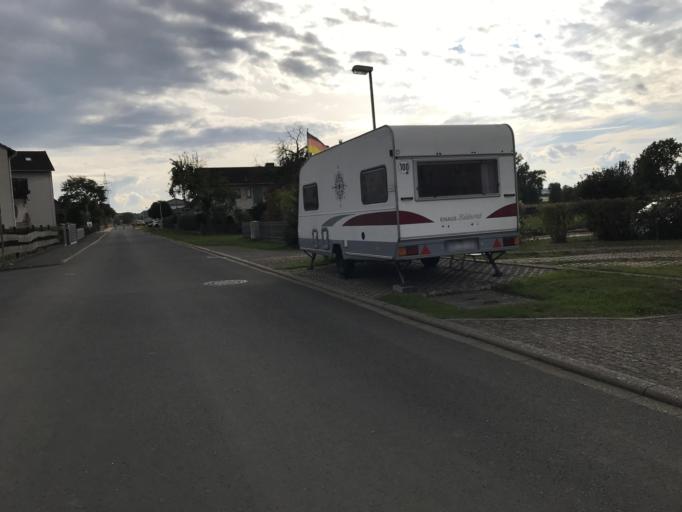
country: DE
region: Hesse
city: Borken
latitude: 51.0576
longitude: 9.3249
